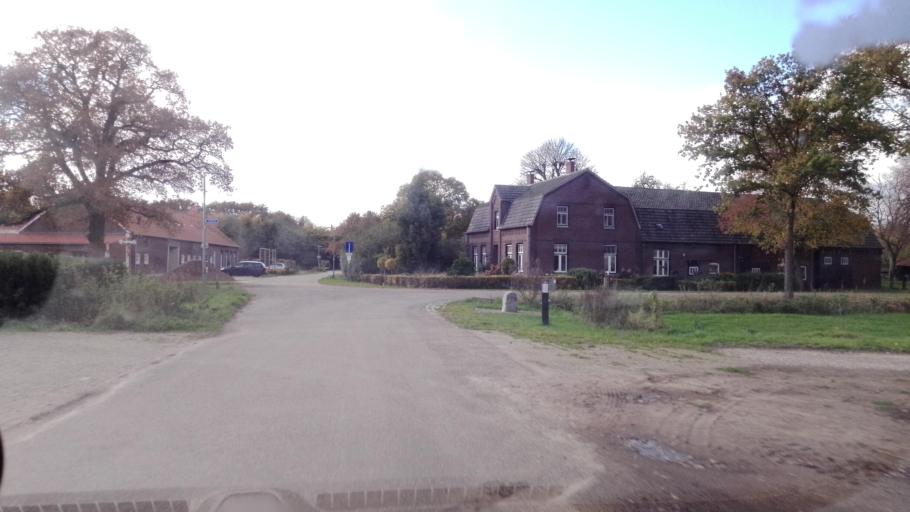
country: NL
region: Limburg
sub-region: Gemeente Venray
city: Venray
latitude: 51.4918
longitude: 6.0415
